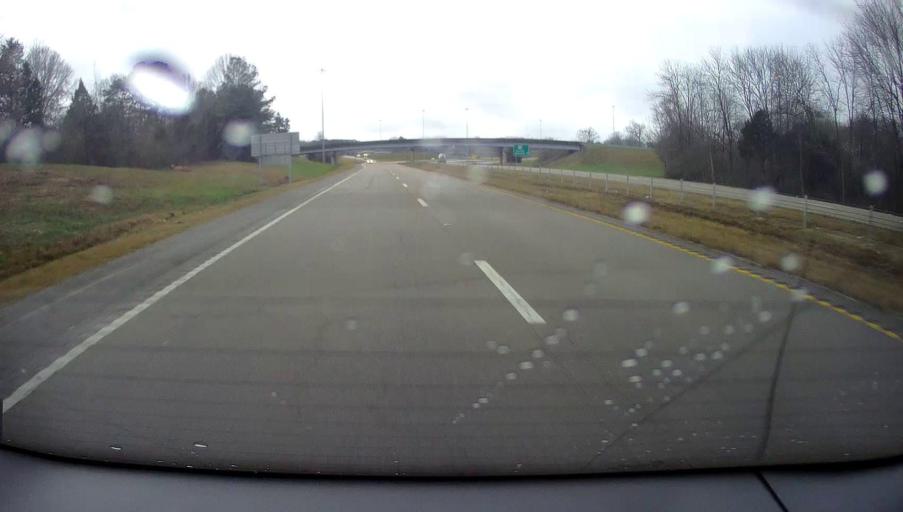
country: US
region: Mississippi
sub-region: Alcorn County
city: Corinth
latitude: 34.9263
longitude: -88.5456
